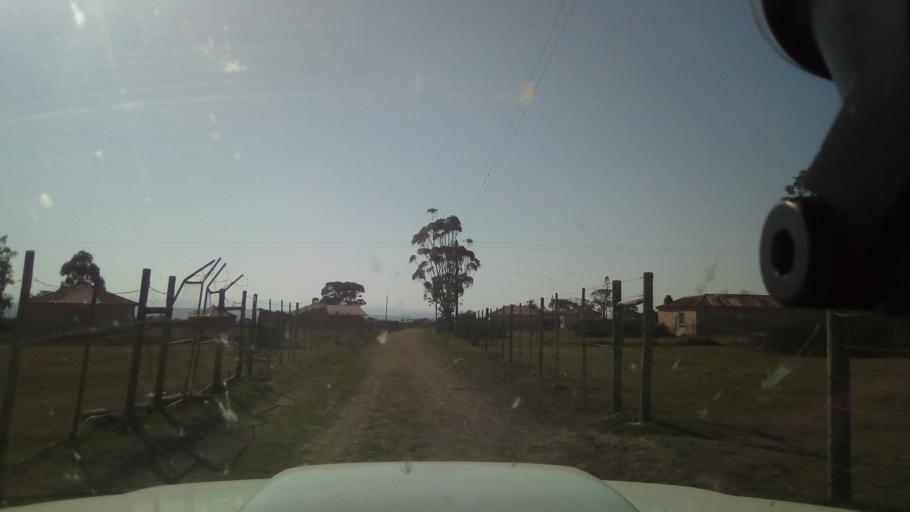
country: ZA
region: Eastern Cape
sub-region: Buffalo City Metropolitan Municipality
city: Bhisho
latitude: -32.9422
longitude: 27.3332
